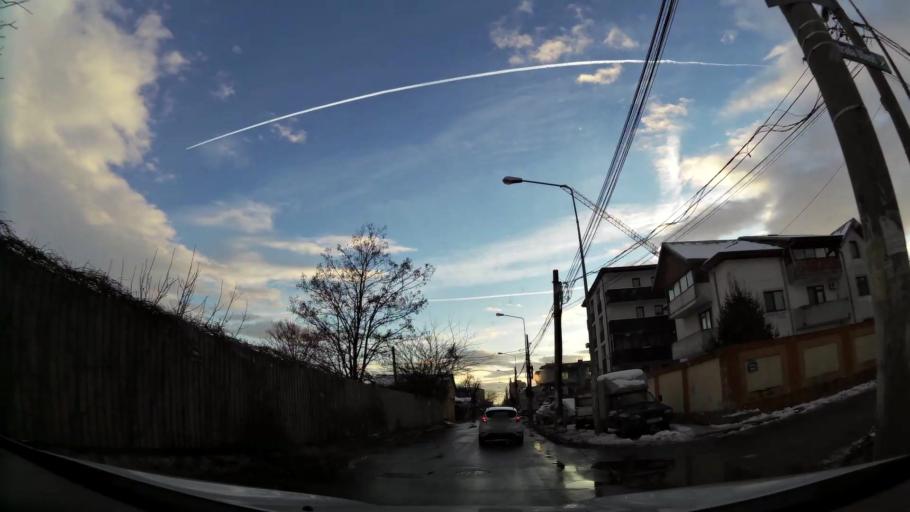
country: RO
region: Ilfov
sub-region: Comuna Popesti-Leordeni
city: Popesti-Leordeni
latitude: 44.3789
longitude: 26.1476
